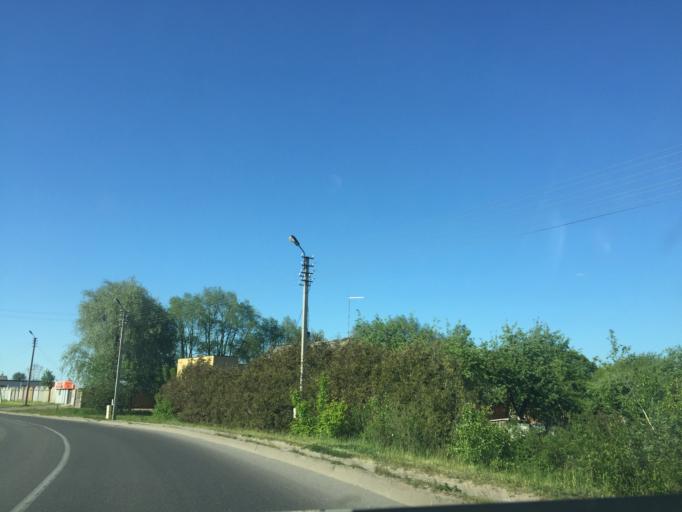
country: LT
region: Panevezys
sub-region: Panevezys City
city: Panevezys
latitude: 55.7468
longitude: 24.3417
